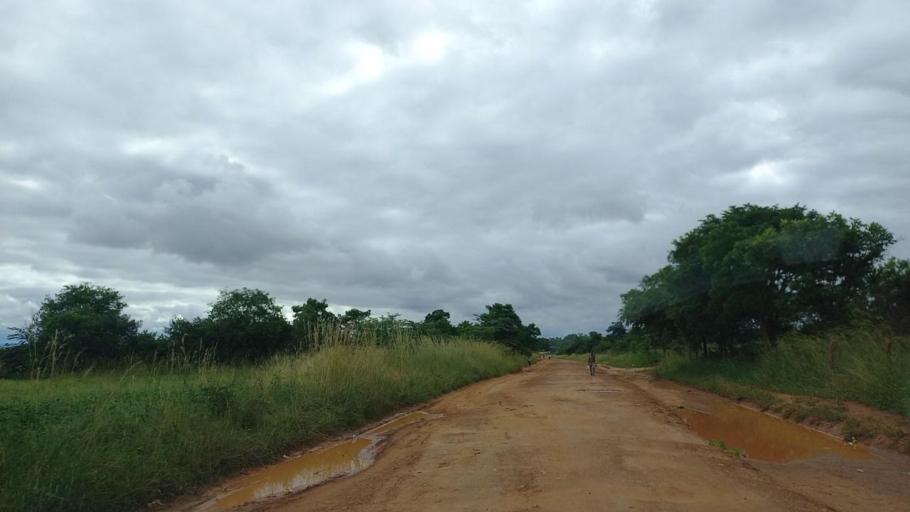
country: ZM
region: Lusaka
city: Chongwe
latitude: -15.4562
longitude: 28.8602
